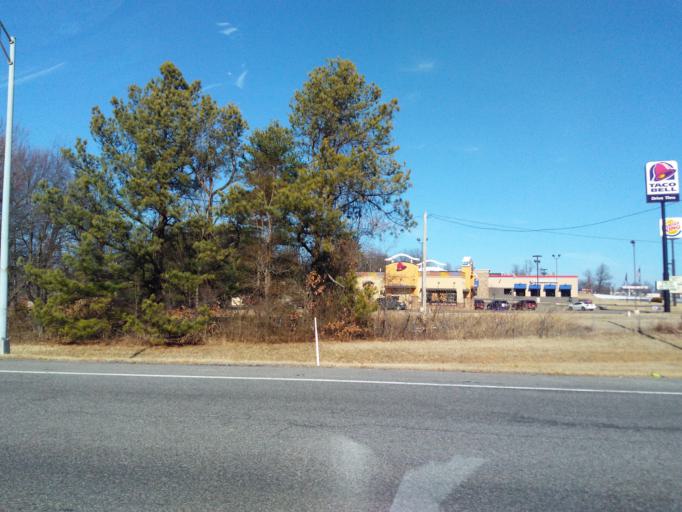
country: US
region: Kentucky
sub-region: McCracken County
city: Hendron
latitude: 37.0527
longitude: -88.6500
